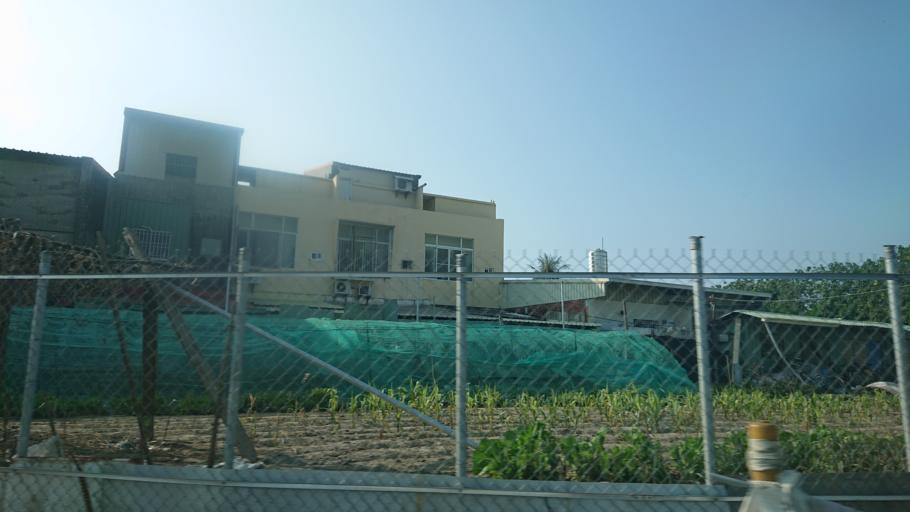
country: TW
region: Taiwan
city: Xinying
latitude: 23.3335
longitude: 120.2504
